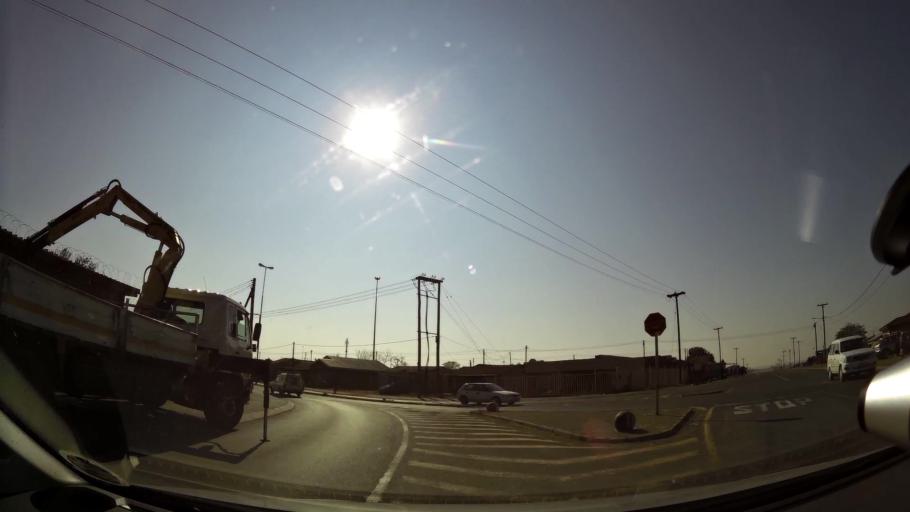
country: ZA
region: Orange Free State
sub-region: Mangaung Metropolitan Municipality
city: Bloemfontein
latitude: -29.1893
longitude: 26.2348
